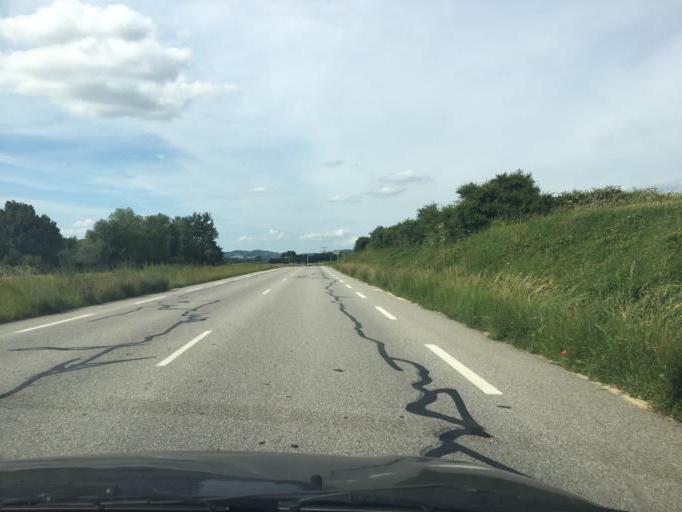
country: FR
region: Rhone-Alpes
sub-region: Departement de la Drome
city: Chanos-Curson
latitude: 45.0753
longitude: 4.9359
